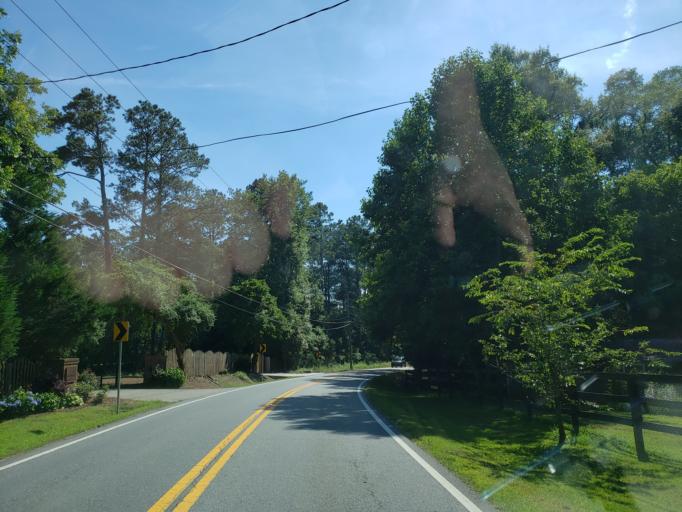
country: US
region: Georgia
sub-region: Cherokee County
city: Woodstock
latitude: 34.1113
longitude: -84.4286
